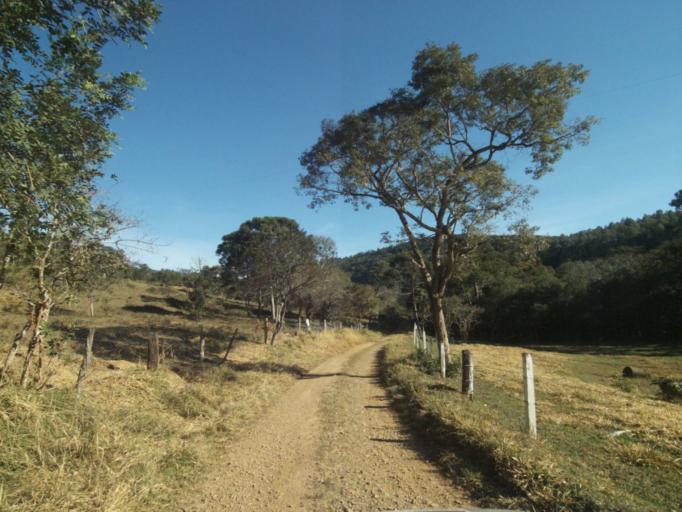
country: BR
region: Parana
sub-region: Tibagi
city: Tibagi
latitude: -24.5557
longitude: -50.5185
